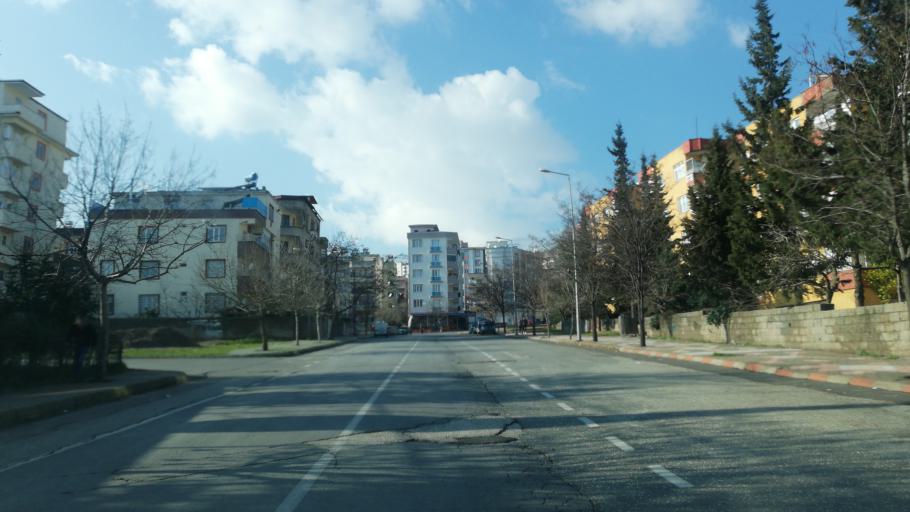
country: TR
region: Kahramanmaras
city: Kahramanmaras
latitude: 37.5894
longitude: 36.9066
